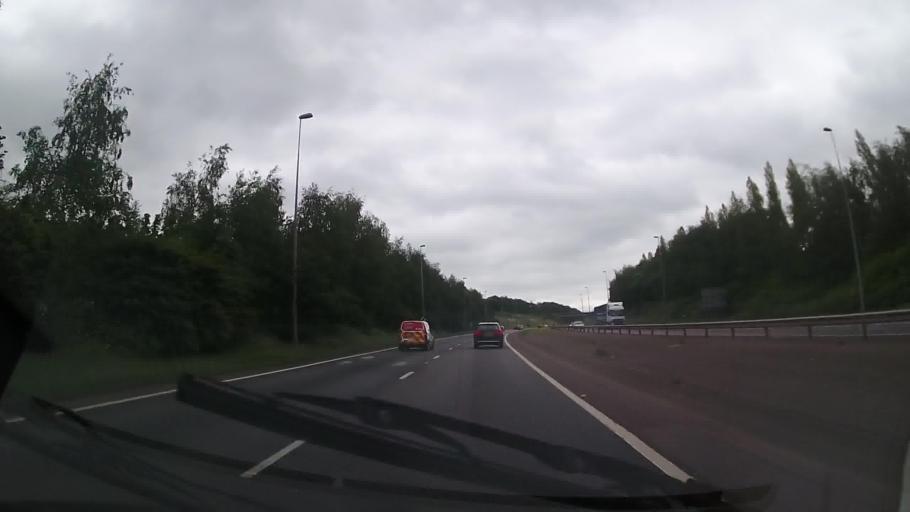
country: GB
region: England
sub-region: Staffordshire
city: Uttoxeter
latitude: 52.9098
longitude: -1.8353
